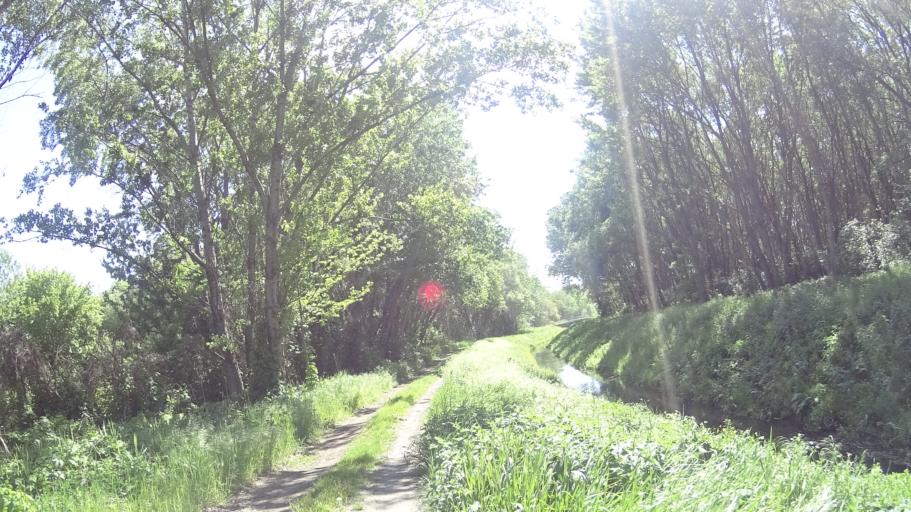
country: HU
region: Budapest
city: Budapest XXIII. keruelet
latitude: 47.3867
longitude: 19.1540
